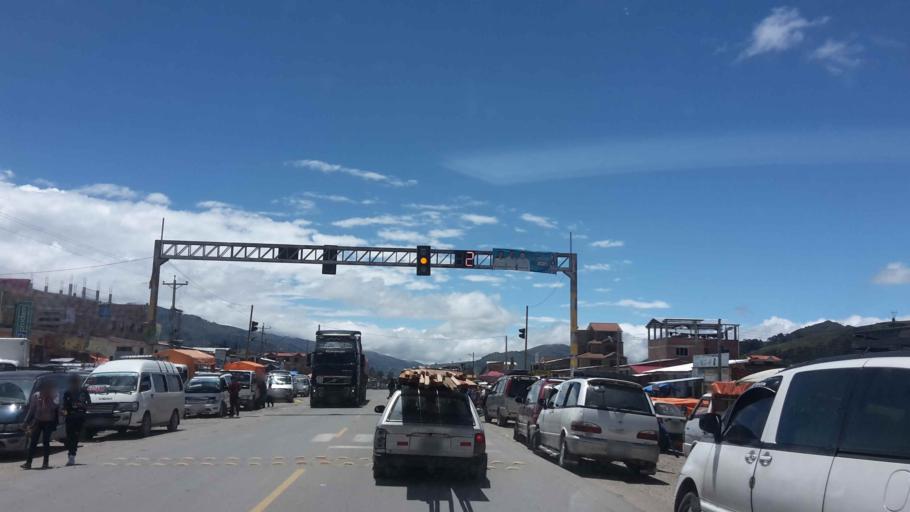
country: BO
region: Cochabamba
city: Colomi
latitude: -17.3368
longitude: -65.8655
